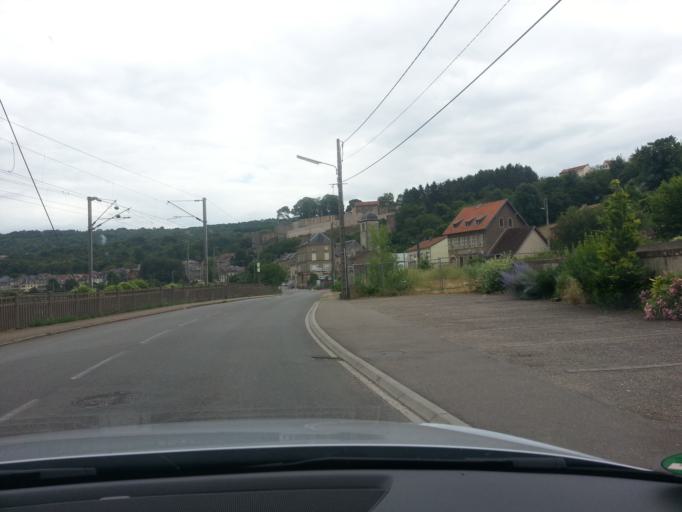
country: FR
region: Lorraine
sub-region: Departement de la Moselle
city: Sierck-les-Bains
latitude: 49.4423
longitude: 6.3529
